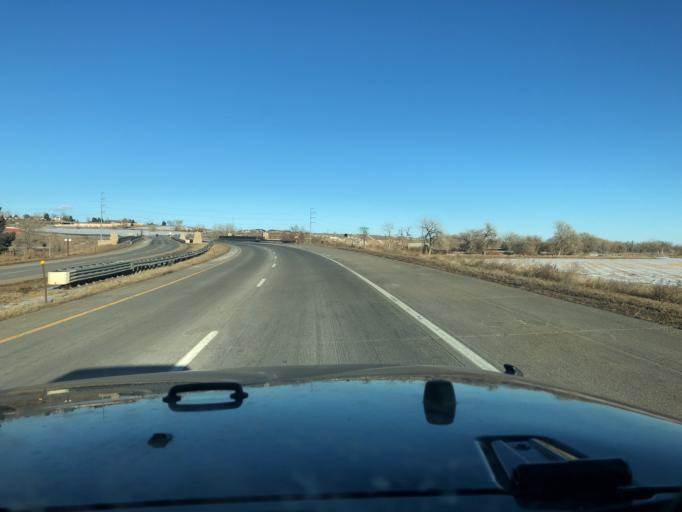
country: US
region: Colorado
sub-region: Boulder County
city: Longmont
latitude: 40.1526
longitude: -105.0794
